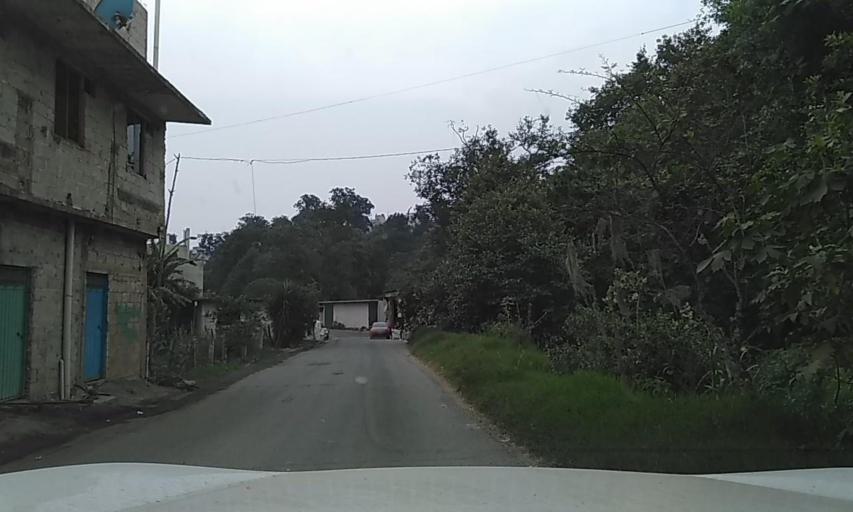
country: MX
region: Veracruz
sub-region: Jilotepec
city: El Pueblito (Garbanzal)
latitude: 19.5722
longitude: -96.8937
